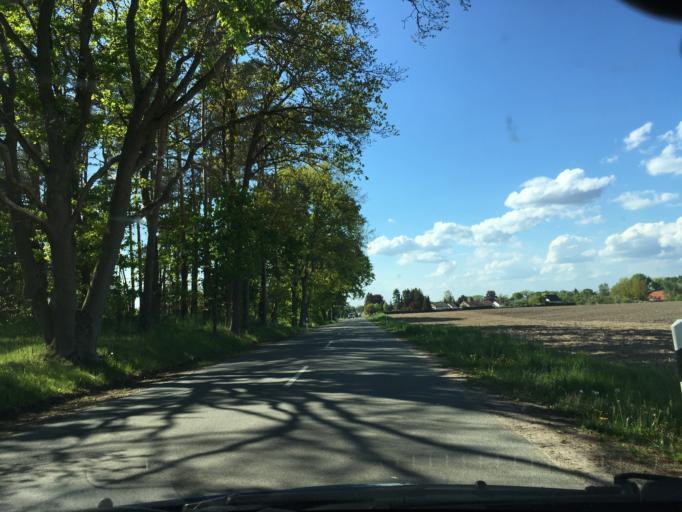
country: DE
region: Lower Saxony
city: Gorleben
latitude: 53.0650
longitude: 11.4122
